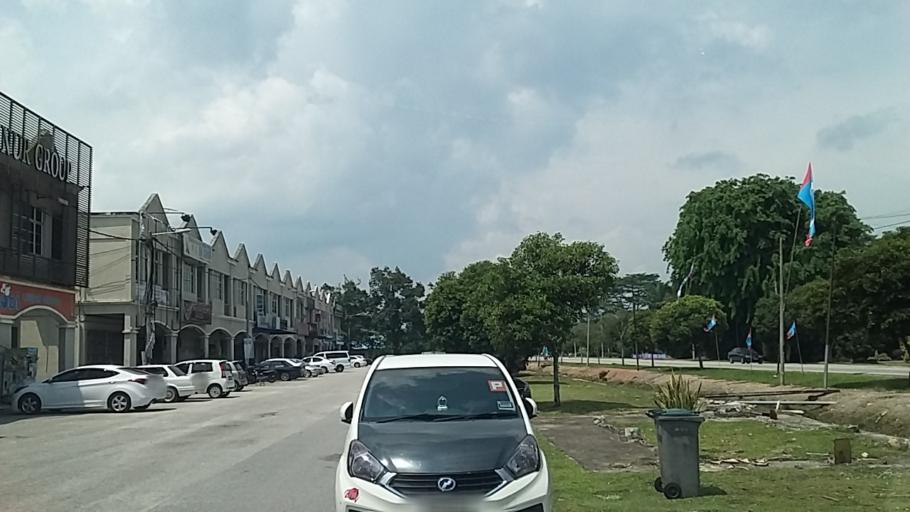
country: MY
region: Johor
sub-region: Daerah Batu Pahat
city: Batu Pahat
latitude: 1.7511
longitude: 103.0305
